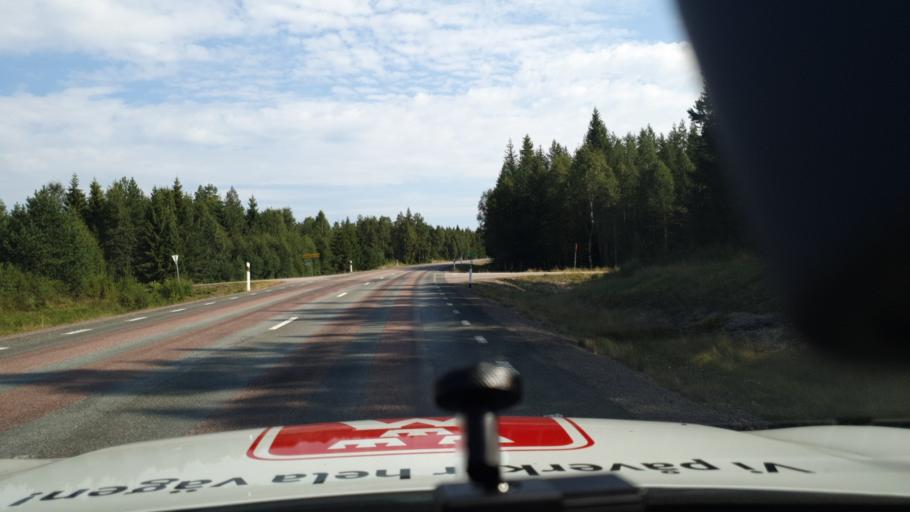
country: SE
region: Dalarna
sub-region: Malung-Saelens kommun
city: Malung
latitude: 60.5134
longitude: 13.4376
